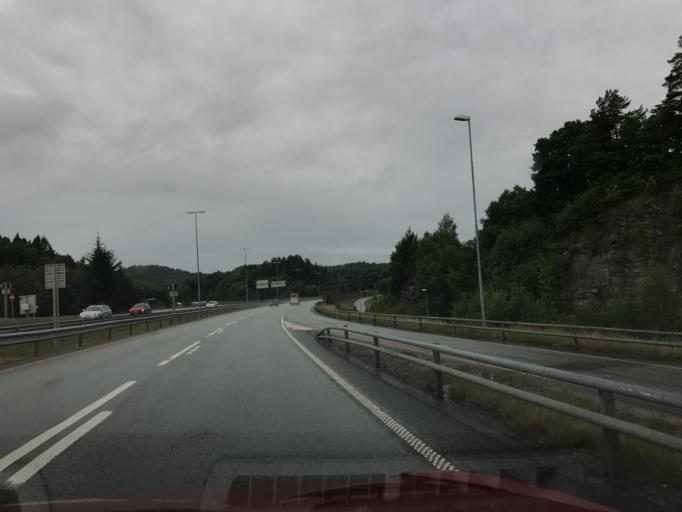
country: NO
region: Vest-Agder
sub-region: Kristiansand
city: Tveit
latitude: 58.1703
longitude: 8.1063
